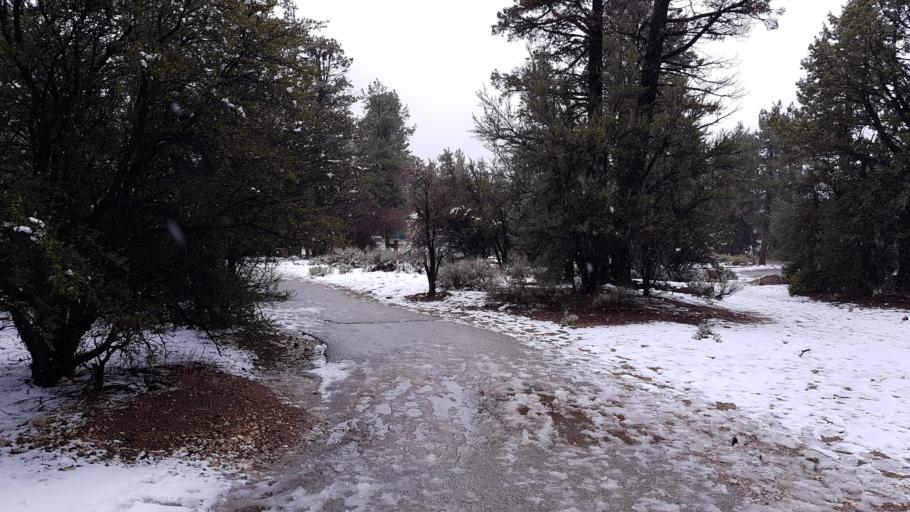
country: US
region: California
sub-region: San Bernardino County
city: Big Bear Lake
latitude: 34.2645
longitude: -116.9107
